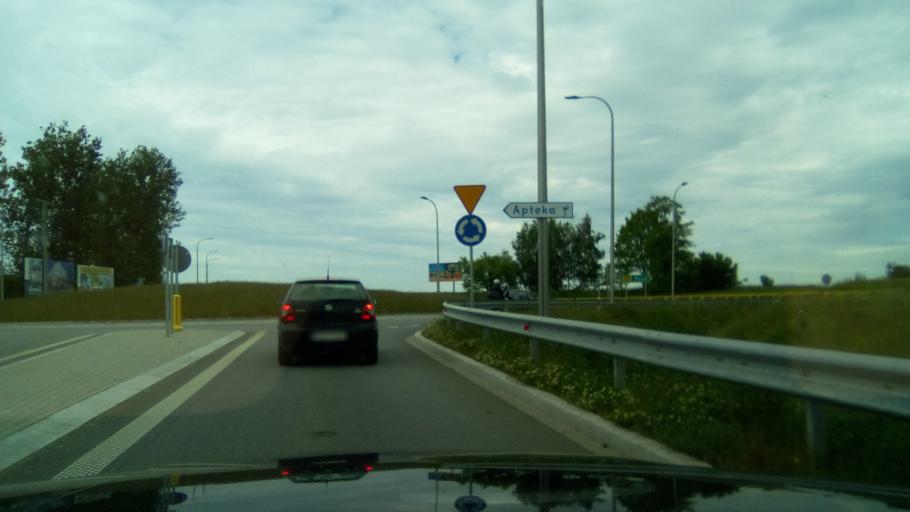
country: PL
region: Pomeranian Voivodeship
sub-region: Powiat leborski
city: Leba
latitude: 54.6750
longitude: 17.6213
